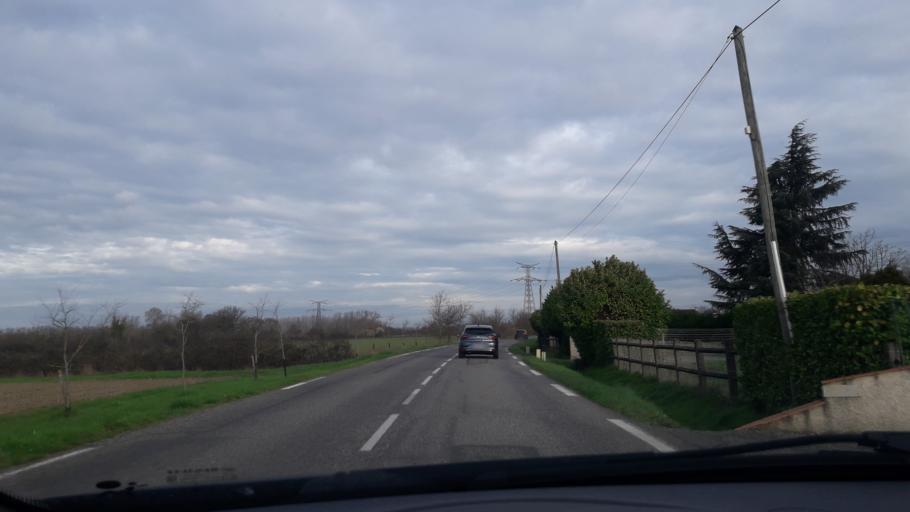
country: FR
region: Midi-Pyrenees
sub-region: Departement de la Haute-Garonne
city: Ondes
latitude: 43.8008
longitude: 1.2934
